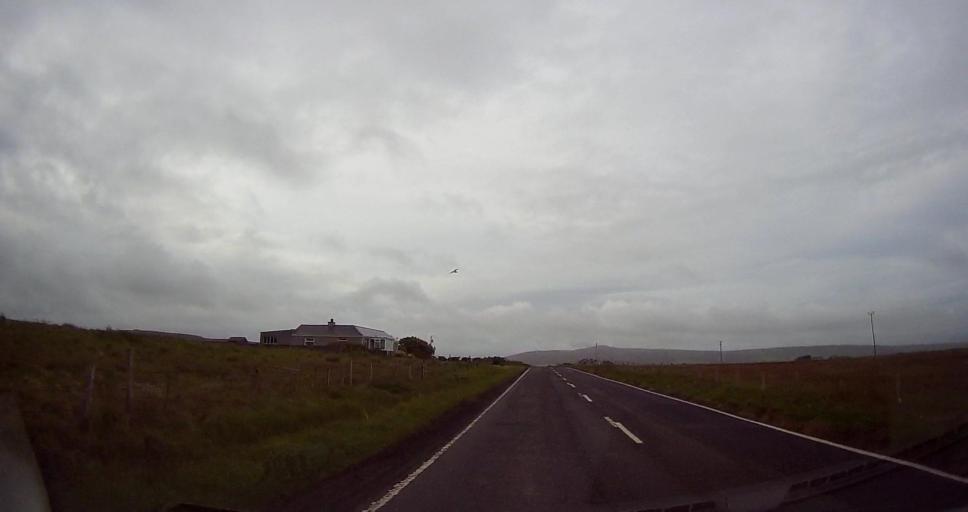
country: GB
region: Scotland
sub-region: Orkney Islands
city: Stromness
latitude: 59.0166
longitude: -3.1566
